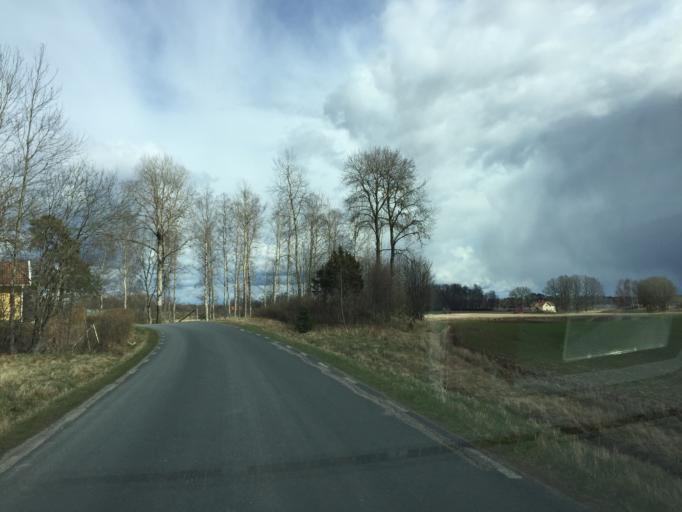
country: SE
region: OErebro
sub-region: Hallsbergs Kommun
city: Palsboda
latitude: 58.9183
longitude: 15.4822
